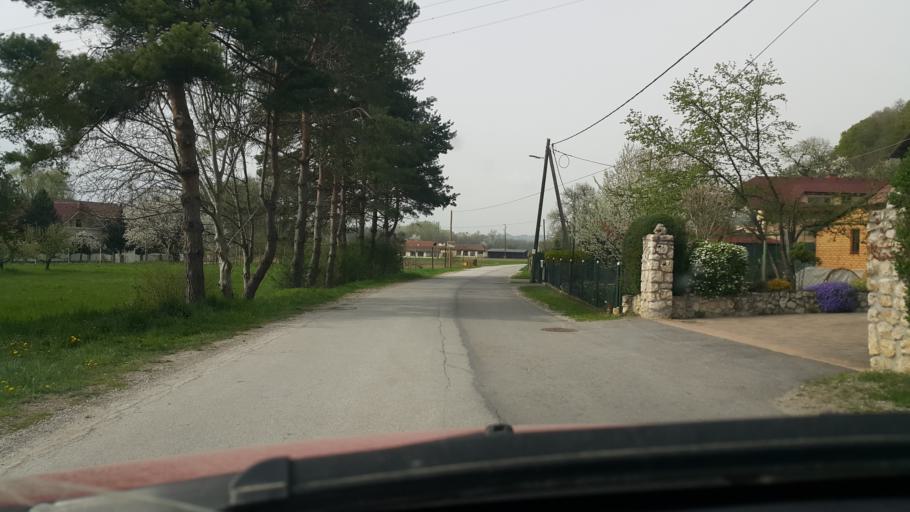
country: SI
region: Duplek
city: Zgornji Duplek
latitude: 46.5173
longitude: 15.7173
